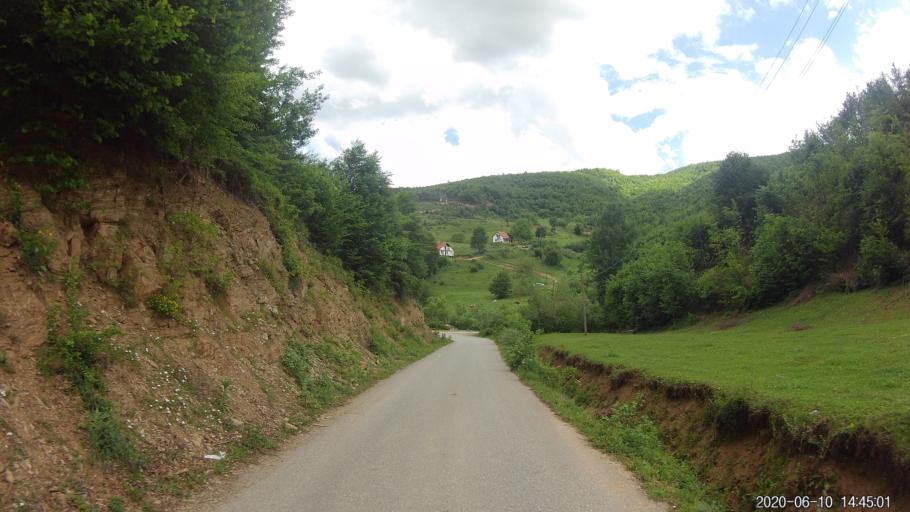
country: XK
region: Prizren
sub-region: Komuna e Therandes
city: Budakovo
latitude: 42.3831
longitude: 20.9490
